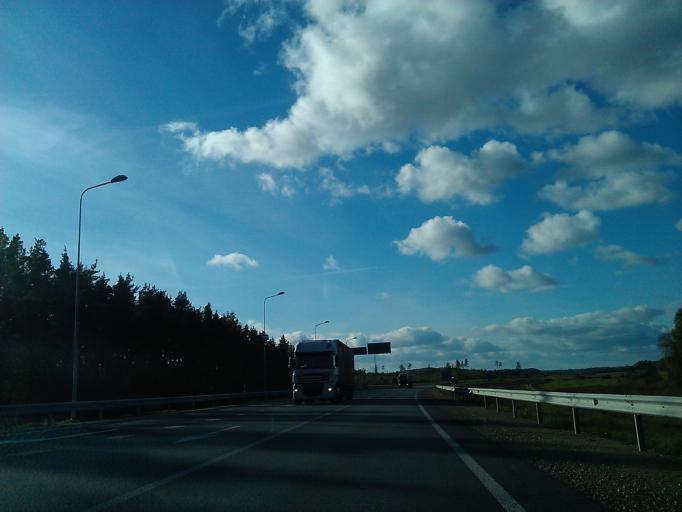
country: LV
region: Koknese
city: Koknese
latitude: 56.6666
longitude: 25.4160
